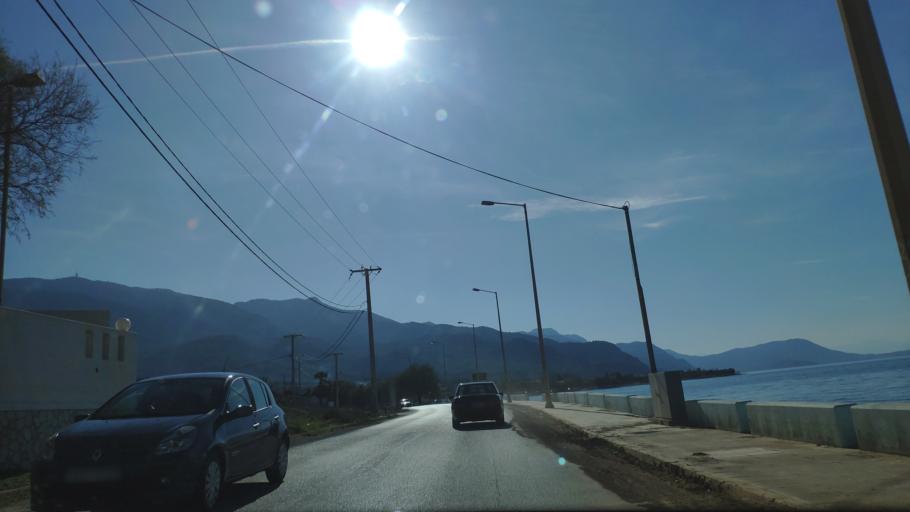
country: GR
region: Attica
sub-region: Nomarchia Dytikis Attikis
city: Kineta
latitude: 38.0756
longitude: 23.1727
